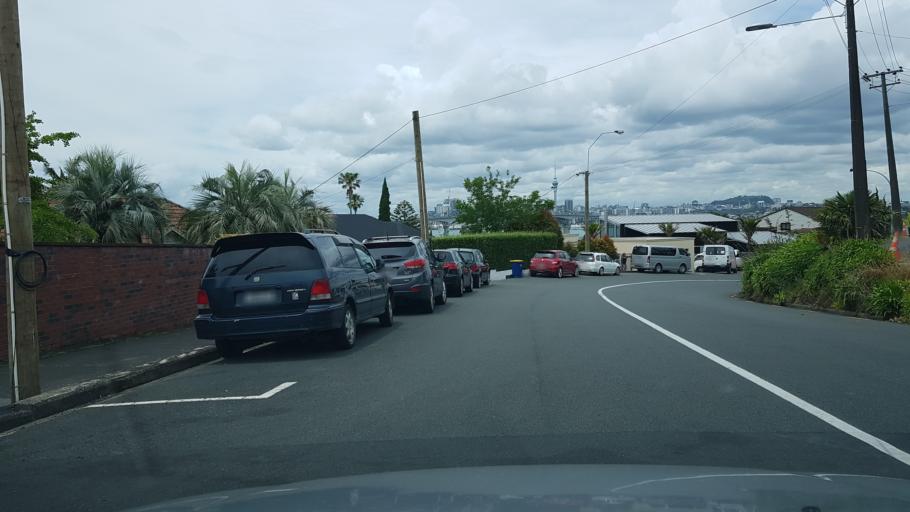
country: NZ
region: Auckland
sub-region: Auckland
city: North Shore
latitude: -36.8200
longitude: 174.7371
